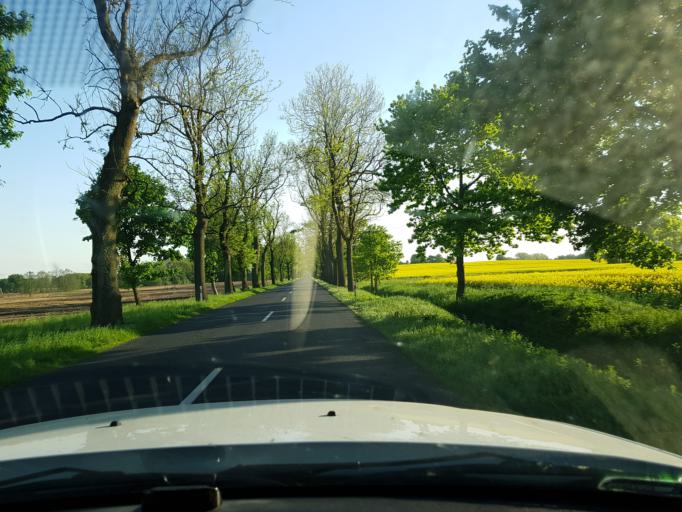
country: PL
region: West Pomeranian Voivodeship
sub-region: Powiat goleniowski
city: Maszewo
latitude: 53.5205
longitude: 15.1037
